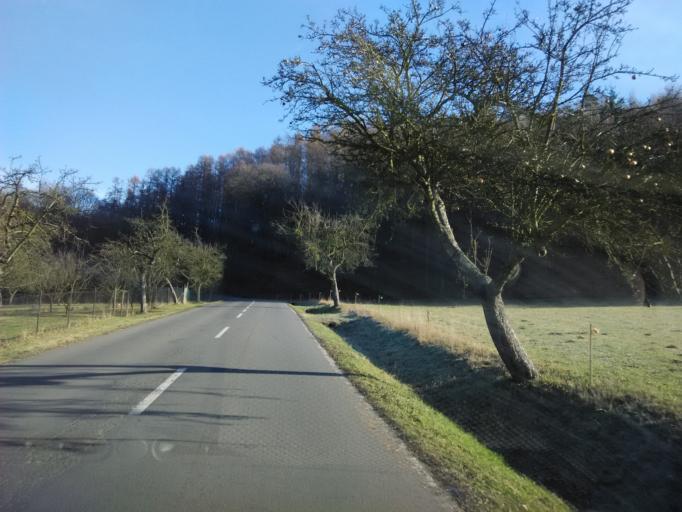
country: CZ
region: Olomoucky
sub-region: Okres Prerov
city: Lipnik nad Becvou
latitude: 49.5121
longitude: 17.6173
